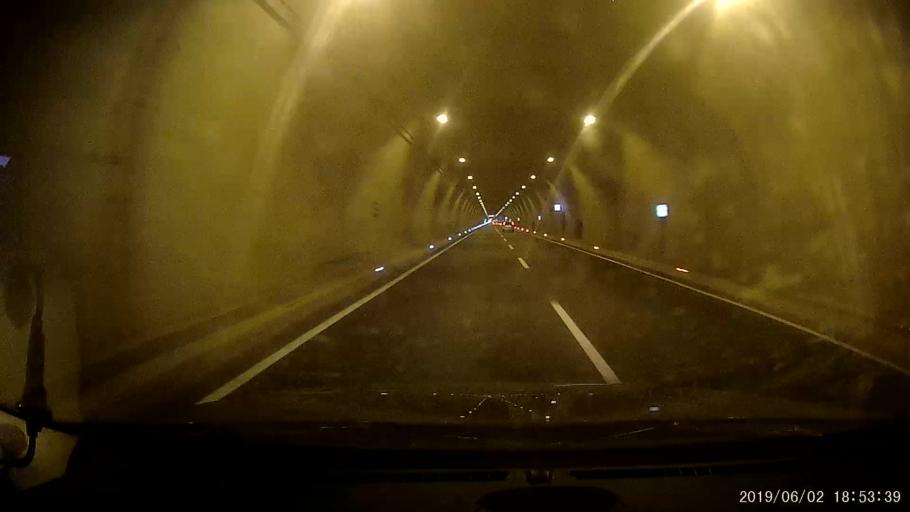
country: TR
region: Ordu
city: Ordu
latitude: 40.9763
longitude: 37.8354
